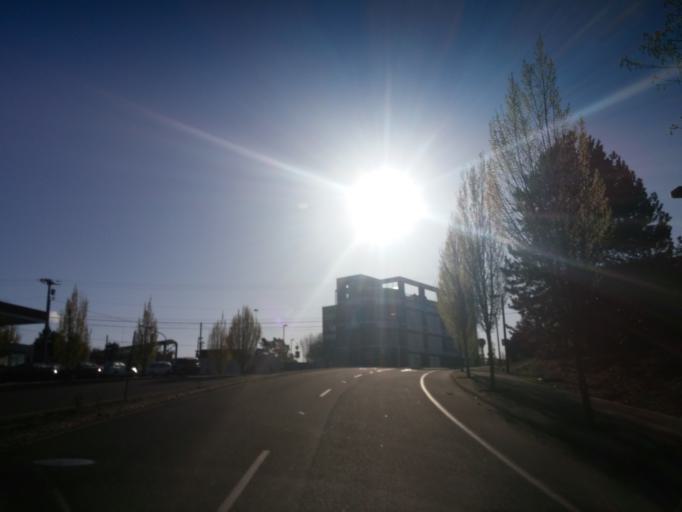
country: US
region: Oregon
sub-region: Washington County
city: Cedar Hills
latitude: 45.5091
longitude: -122.7846
